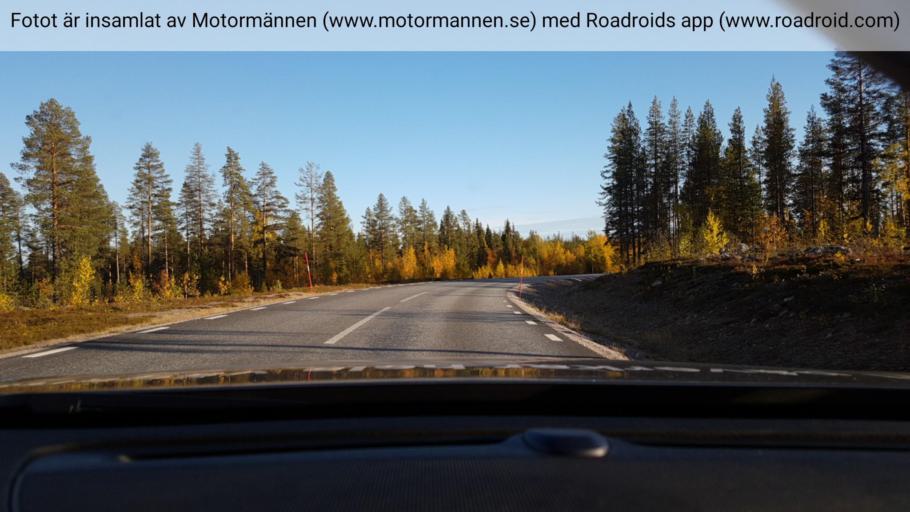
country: SE
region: Norrbotten
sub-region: Jokkmokks Kommun
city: Jokkmokk
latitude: 66.7964
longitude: 19.8802
